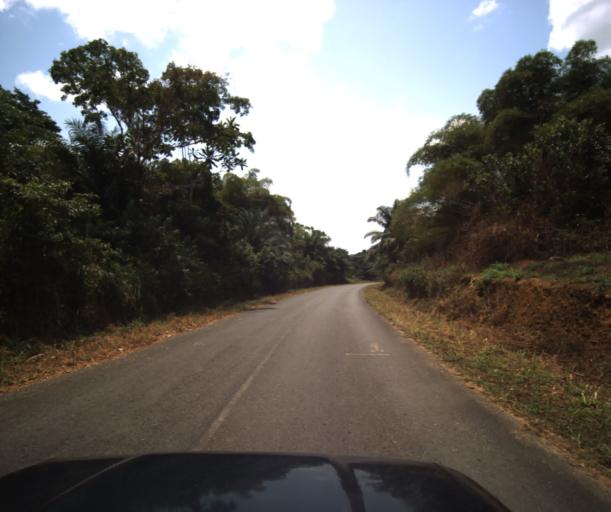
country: CM
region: Centre
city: Eseka
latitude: 3.6961
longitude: 10.7867
